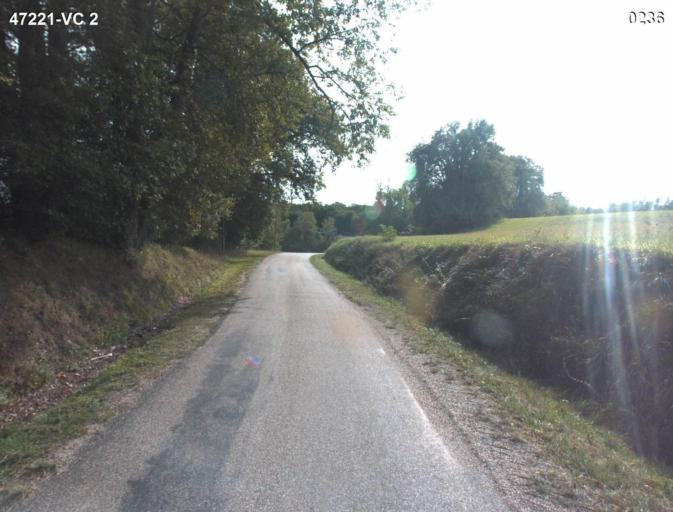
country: FR
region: Aquitaine
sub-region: Departement du Lot-et-Garonne
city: Mezin
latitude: 44.1078
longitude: 0.2366
